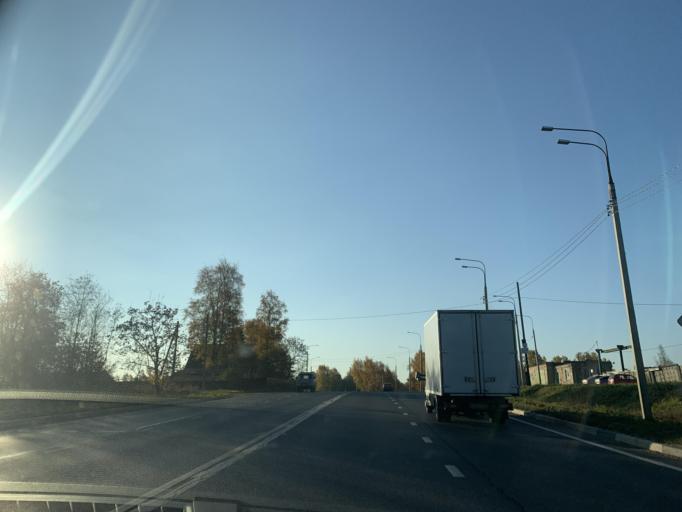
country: RU
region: Jaroslavl
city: Konstantinovskiy
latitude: 57.7616
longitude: 39.6848
